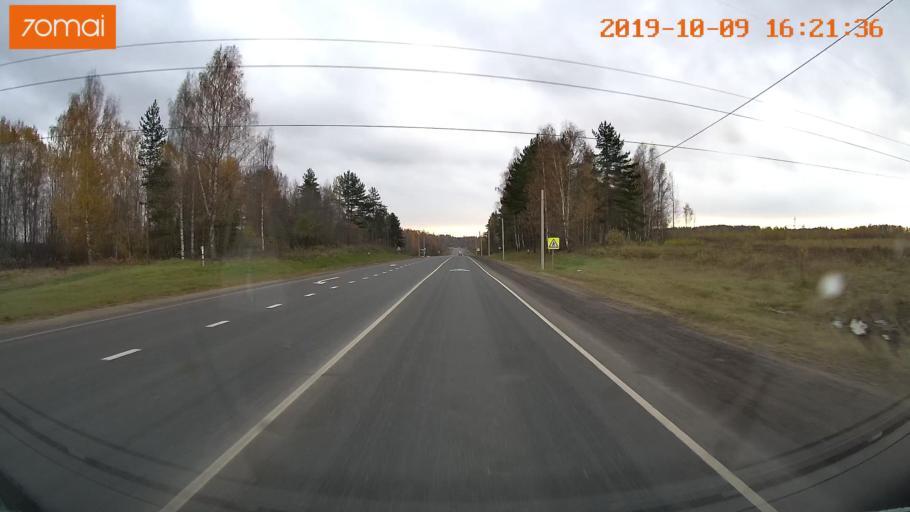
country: RU
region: Kostroma
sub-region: Kostromskoy Rayon
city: Kostroma
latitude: 57.6894
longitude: 40.8886
